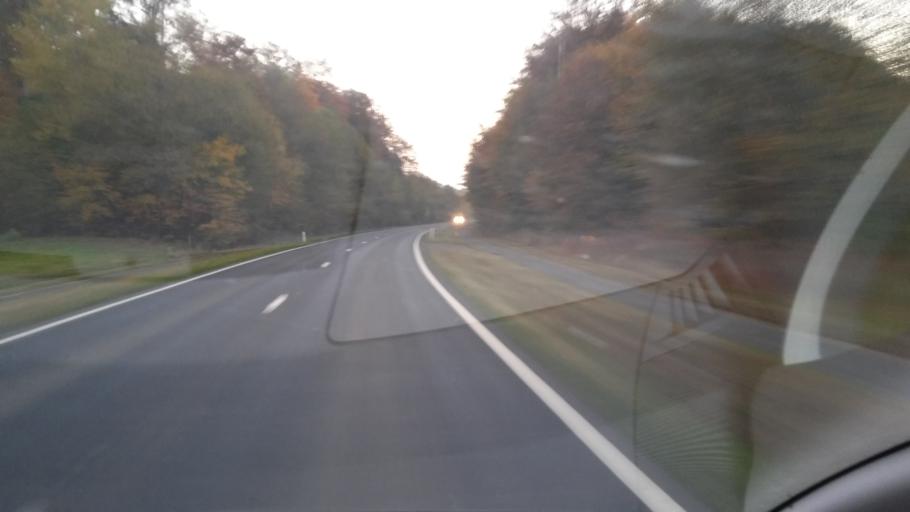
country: BE
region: Wallonia
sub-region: Province du Luxembourg
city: Etalle
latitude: 49.6493
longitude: 5.5803
